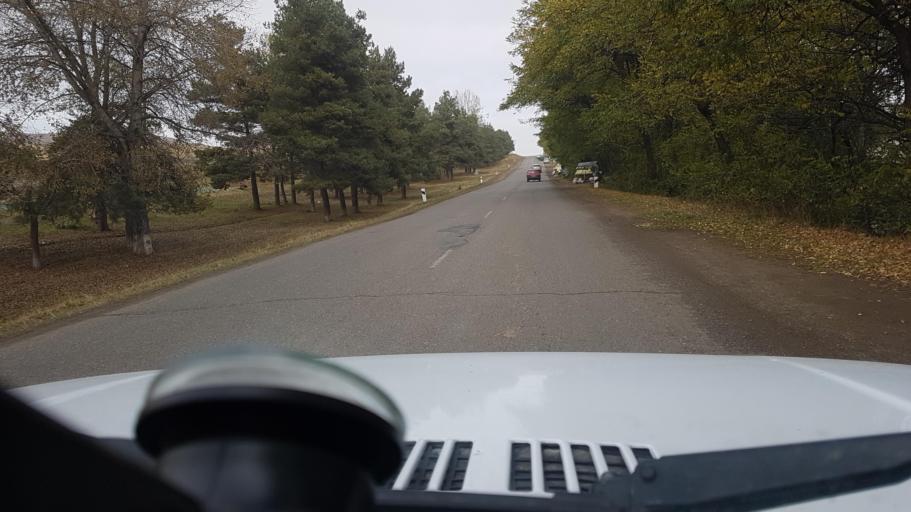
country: AZ
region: Gadabay Rayon
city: Ariqdam
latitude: 40.6352
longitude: 45.8131
